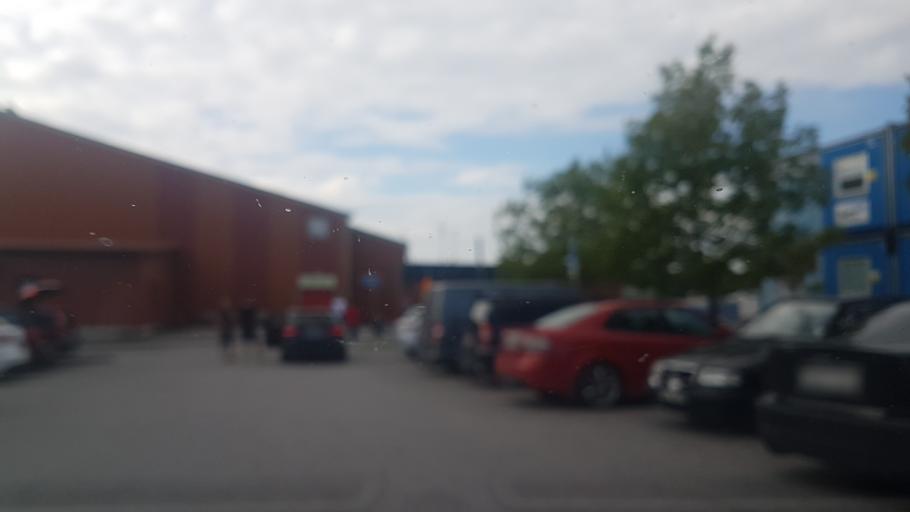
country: SE
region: Stockholm
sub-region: Jarfalla Kommun
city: Jakobsberg
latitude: 59.4184
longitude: 17.8251
